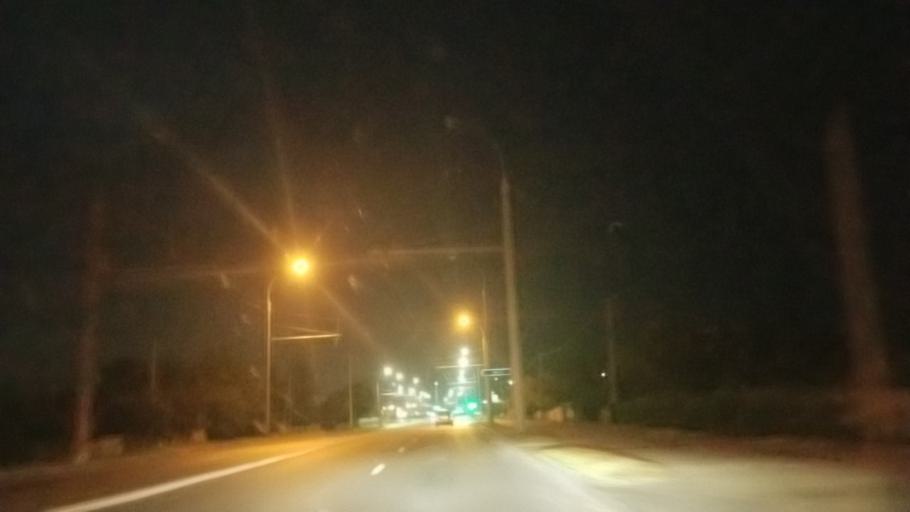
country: BY
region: Brest
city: Brest
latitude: 52.0750
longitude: 23.7665
